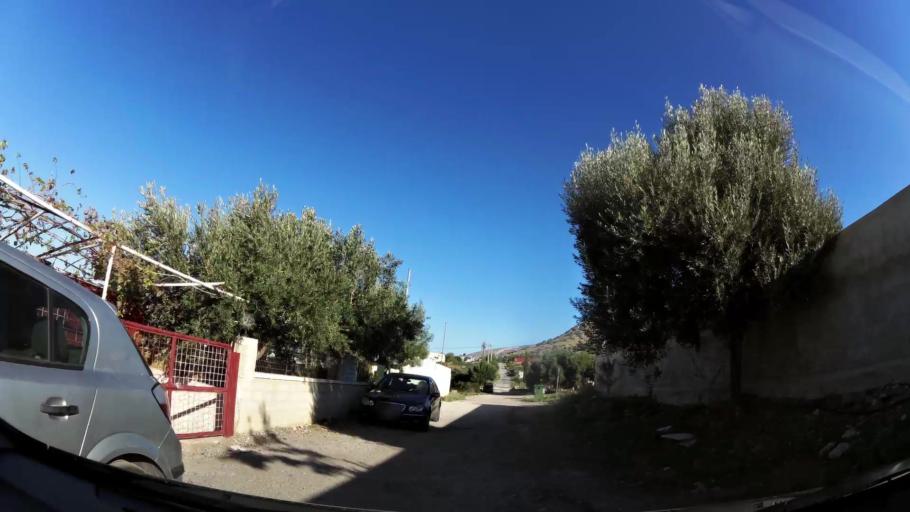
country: GR
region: Attica
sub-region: Nomarchia Athinas
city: Glyfada
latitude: 37.8720
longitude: 23.7754
